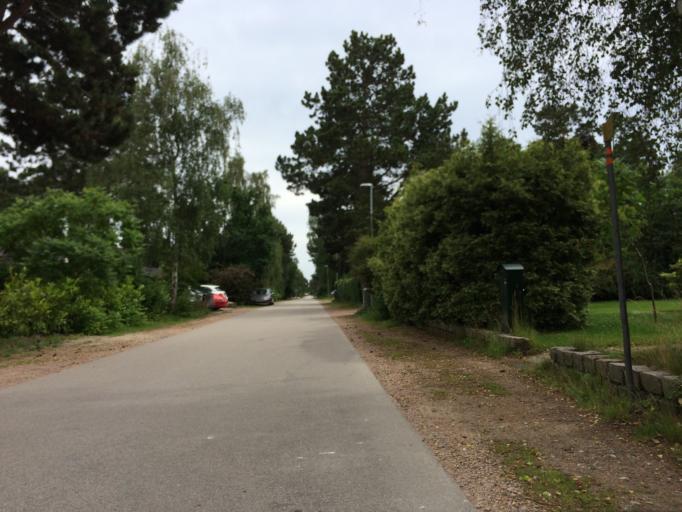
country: SE
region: Skane
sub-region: Vellinge Kommun
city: Ljunghusen
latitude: 55.4033
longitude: 12.9299
